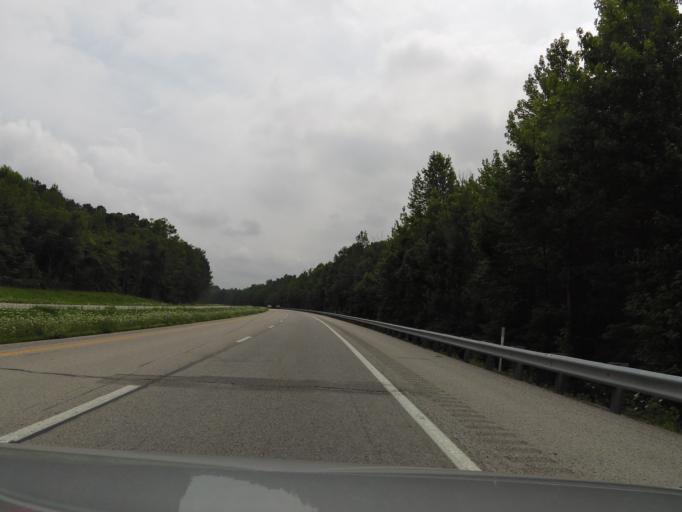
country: US
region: Kentucky
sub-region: Ohio County
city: Beaver Dam
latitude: 37.3523
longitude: -86.8973
